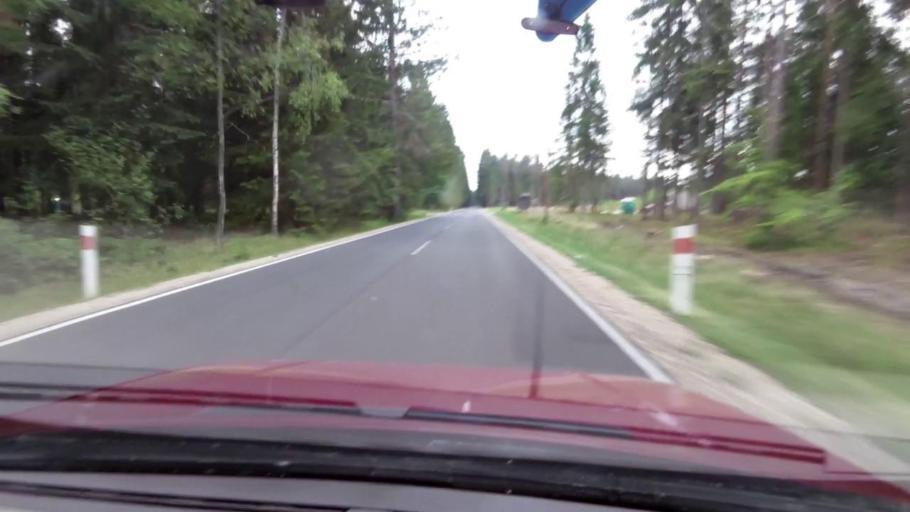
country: PL
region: West Pomeranian Voivodeship
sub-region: Powiat koszalinski
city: Polanow
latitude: 54.1428
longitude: 16.4862
